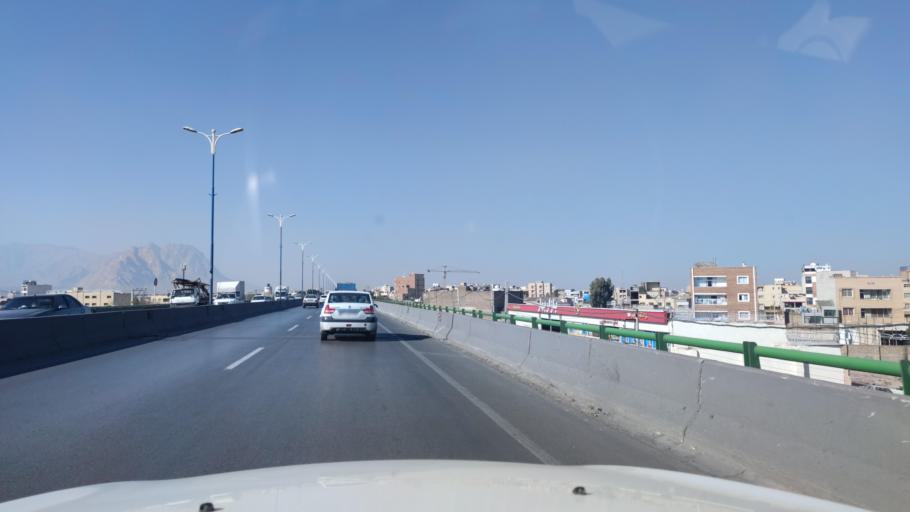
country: IR
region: Isfahan
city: Rehnan
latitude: 32.7019
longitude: 51.6150
